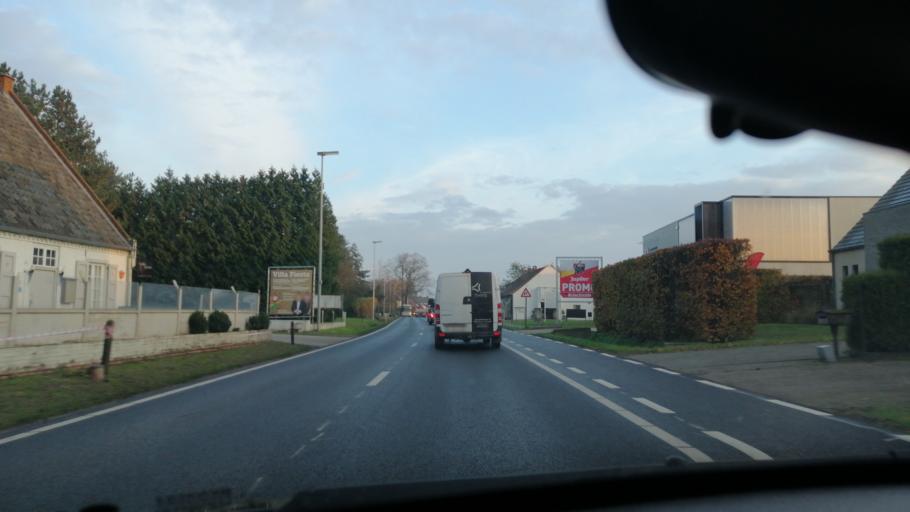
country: BE
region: Flanders
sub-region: Provincie Antwerpen
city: Lille
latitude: 51.2534
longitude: 4.8119
